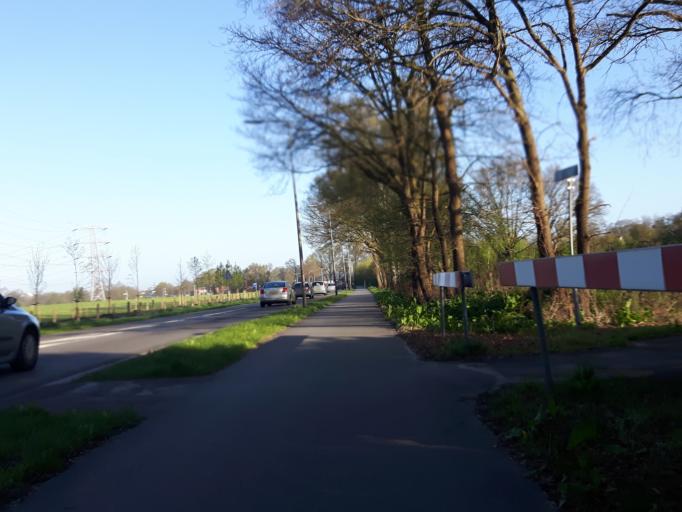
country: NL
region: Overijssel
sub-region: Gemeente Enschede
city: Enschede
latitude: 52.2102
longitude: 6.8475
